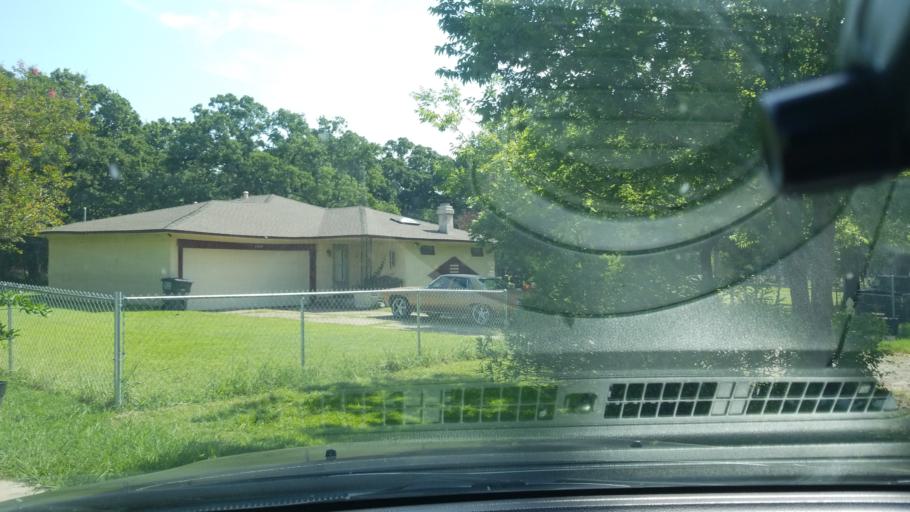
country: US
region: Texas
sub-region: Dallas County
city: Balch Springs
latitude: 32.7240
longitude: -96.6307
